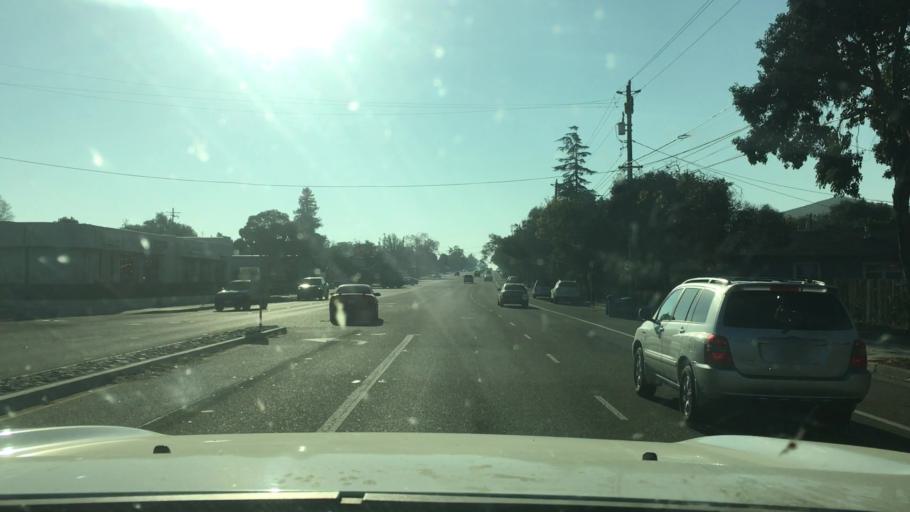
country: US
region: California
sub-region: San Luis Obispo County
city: San Luis Obispo
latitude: 35.2683
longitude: -120.6554
